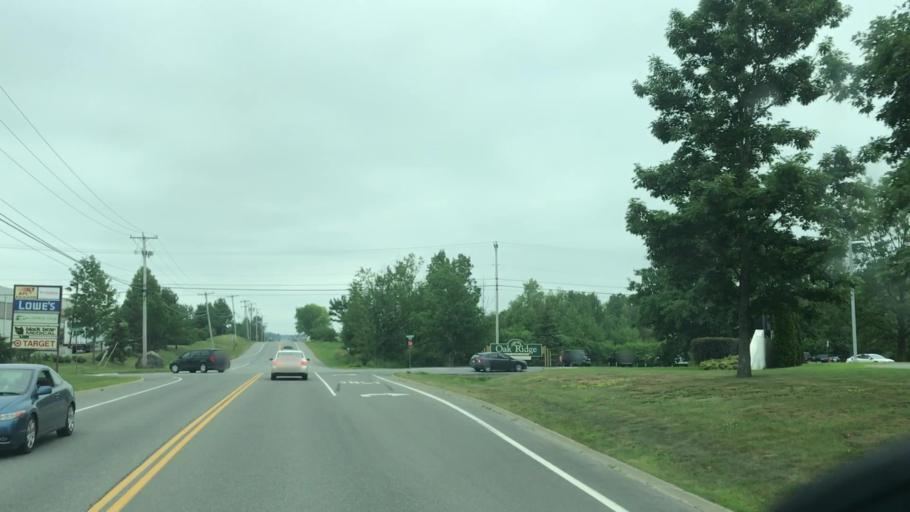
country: US
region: Maine
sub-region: Penobscot County
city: Veazie
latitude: 44.8454
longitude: -68.7406
